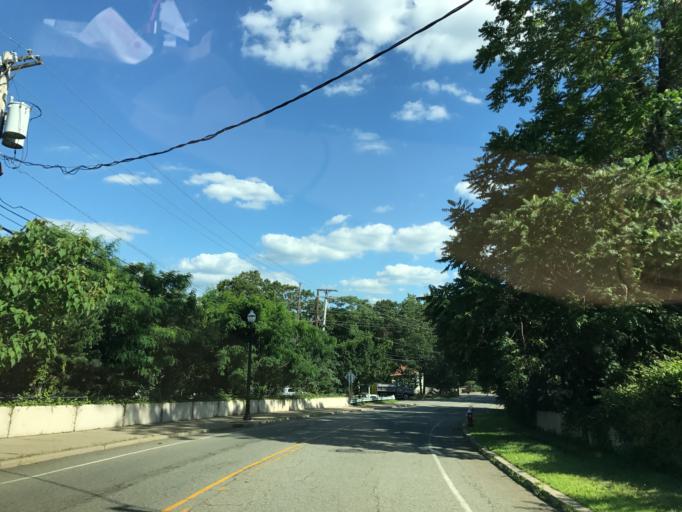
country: US
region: New Jersey
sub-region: Morris County
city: Boonton
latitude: 40.8965
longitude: -74.4173
